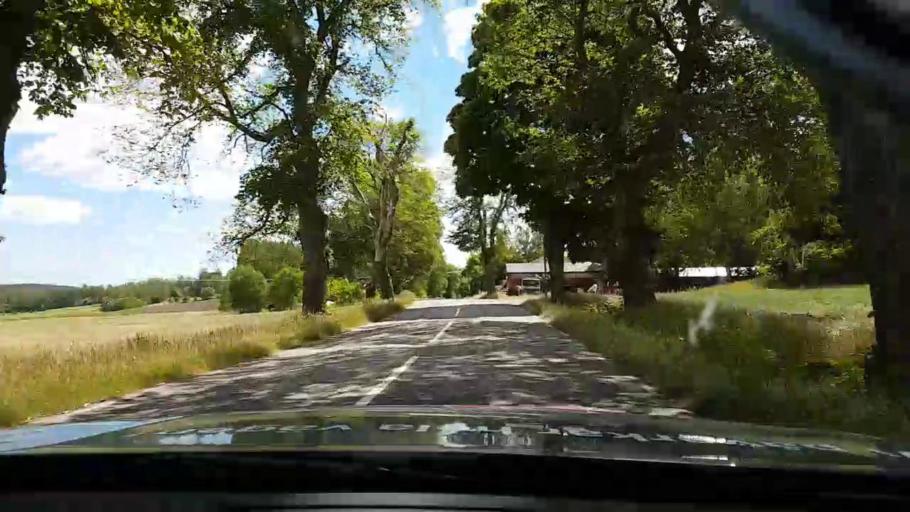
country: SE
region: Kalmar
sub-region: Vasterviks Kommun
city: Forserum
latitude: 58.0069
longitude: 16.4846
